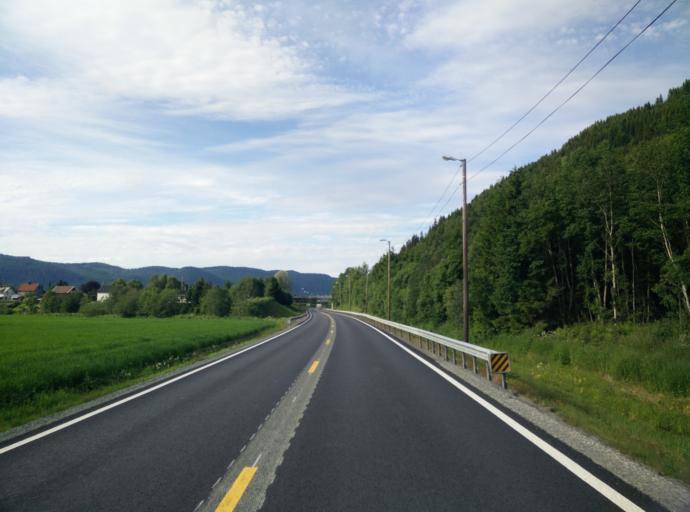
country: NO
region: Sor-Trondelag
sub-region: Orkdal
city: Orkanger
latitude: 63.2896
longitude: 9.8521
